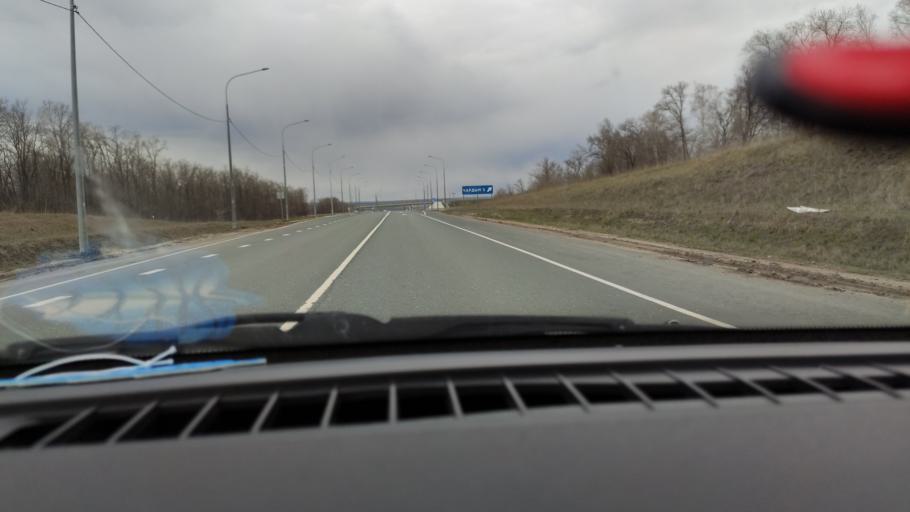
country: RU
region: Saratov
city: Yelshanka
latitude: 51.8253
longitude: 46.2944
